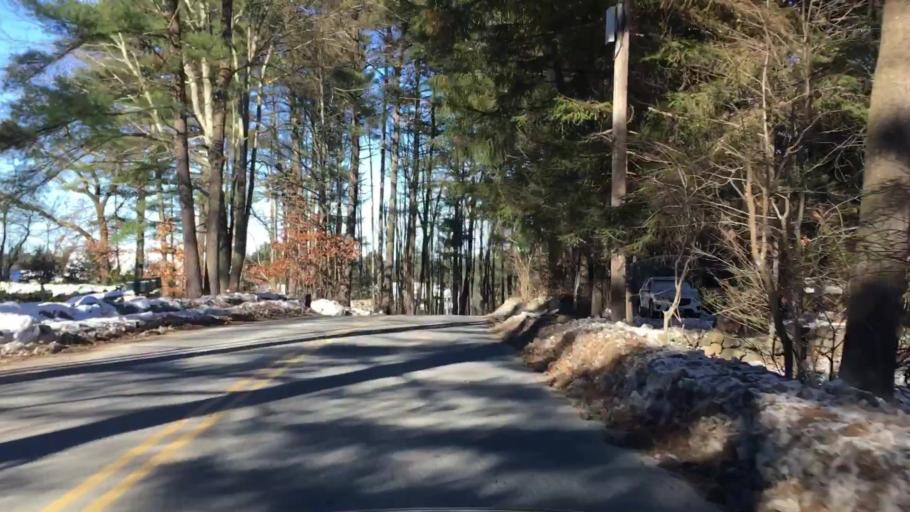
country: US
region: New Hampshire
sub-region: Hillsborough County
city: Milford
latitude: 42.8199
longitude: -71.6333
